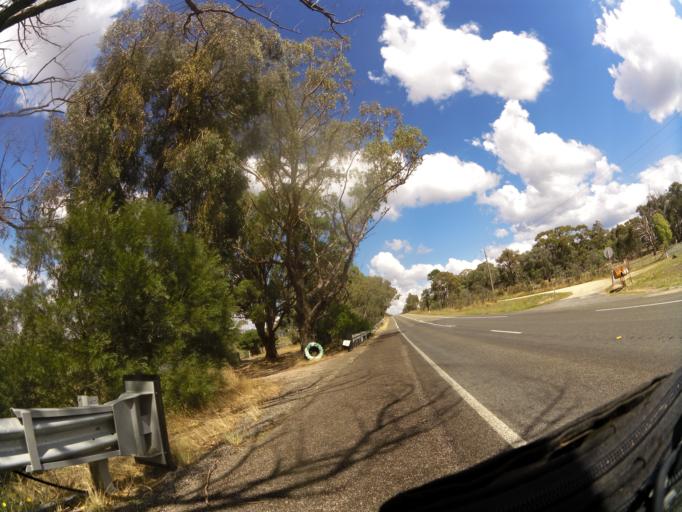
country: AU
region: Victoria
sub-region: Benalla
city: Benalla
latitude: -36.7893
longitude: 146.0107
